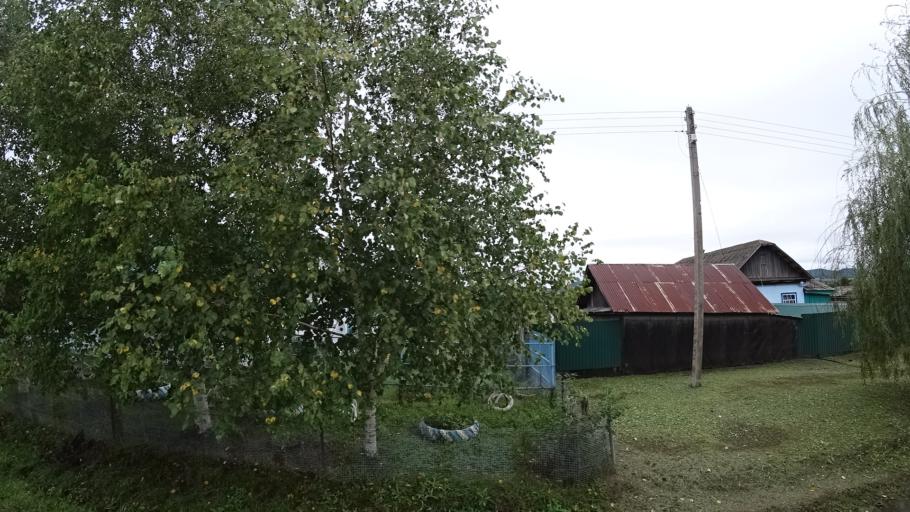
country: RU
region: Primorskiy
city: Monastyrishche
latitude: 44.1896
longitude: 132.4889
